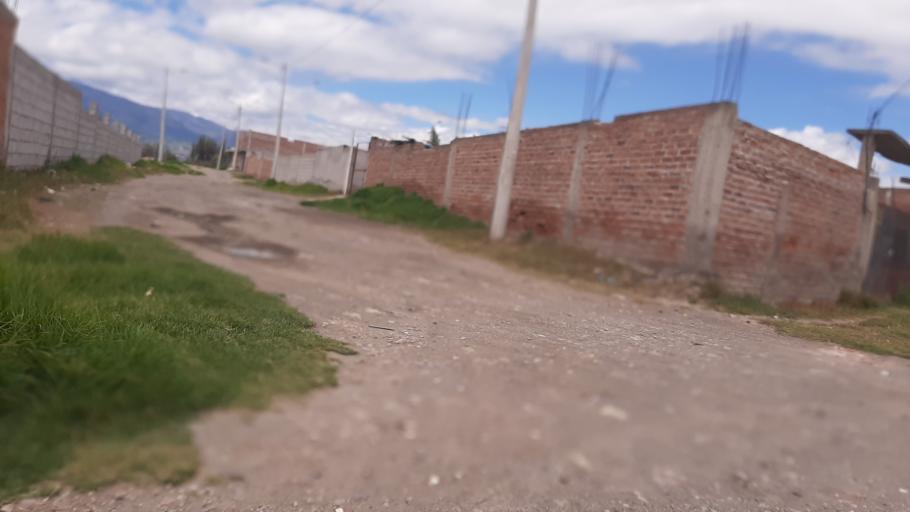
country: EC
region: Chimborazo
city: Riobamba
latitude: -1.6520
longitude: -78.6403
